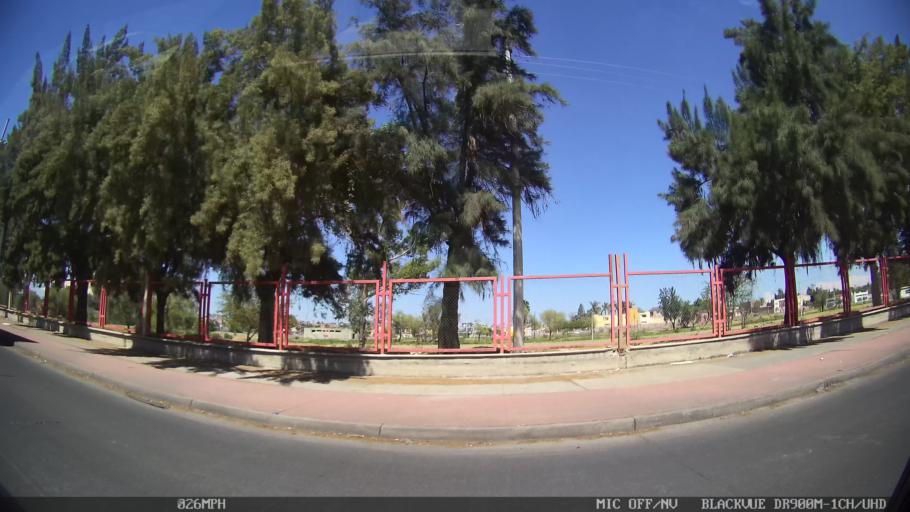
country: MX
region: Jalisco
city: Tlaquepaque
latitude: 20.6539
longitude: -103.2712
